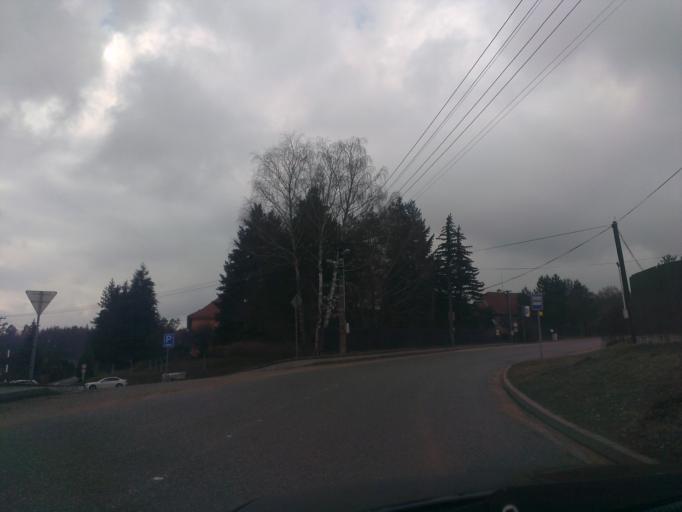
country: CZ
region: South Moravian
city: Bilovice nad Svitavou
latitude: 49.2642
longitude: 16.7118
